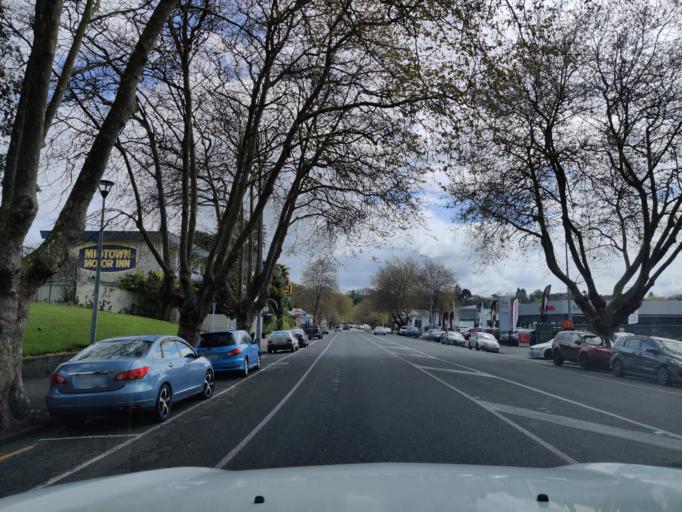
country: NZ
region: Manawatu-Wanganui
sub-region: Wanganui District
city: Wanganui
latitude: -39.9276
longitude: 175.0430
